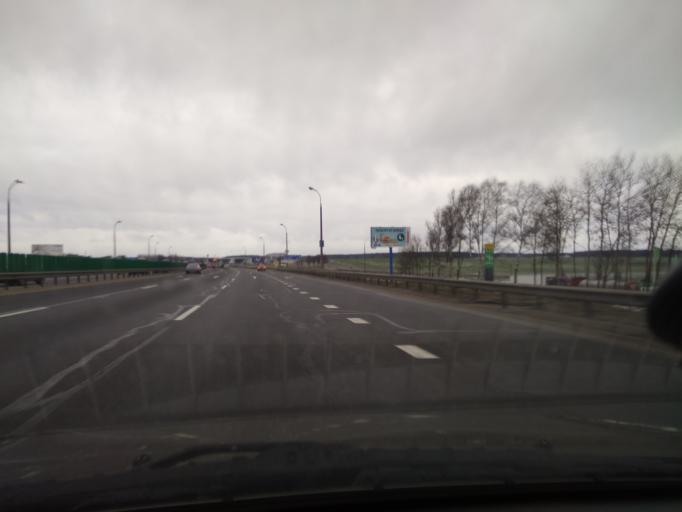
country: BY
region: Minsk
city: Bal'shavik
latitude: 53.9694
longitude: 27.6006
